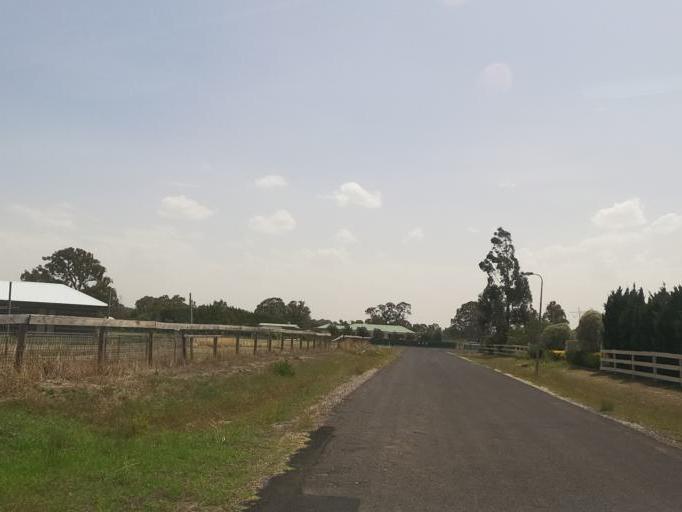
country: AU
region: Victoria
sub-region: Hume
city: Craigieburn
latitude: -37.5517
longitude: 144.9007
